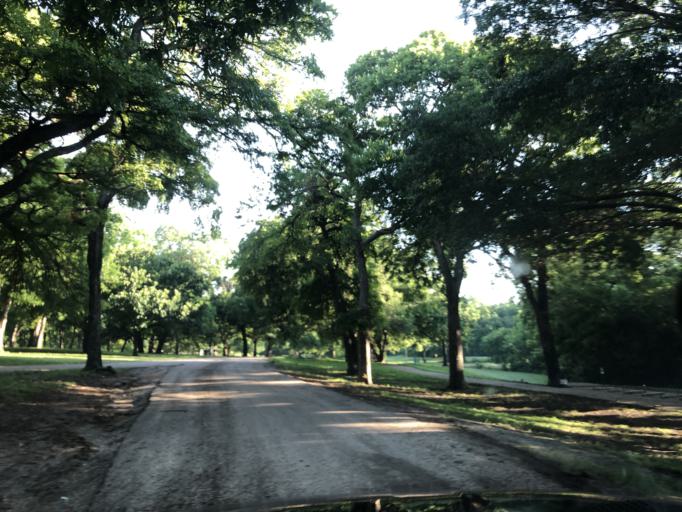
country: US
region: Texas
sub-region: Dallas County
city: Garland
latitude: 32.8472
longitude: -96.6128
